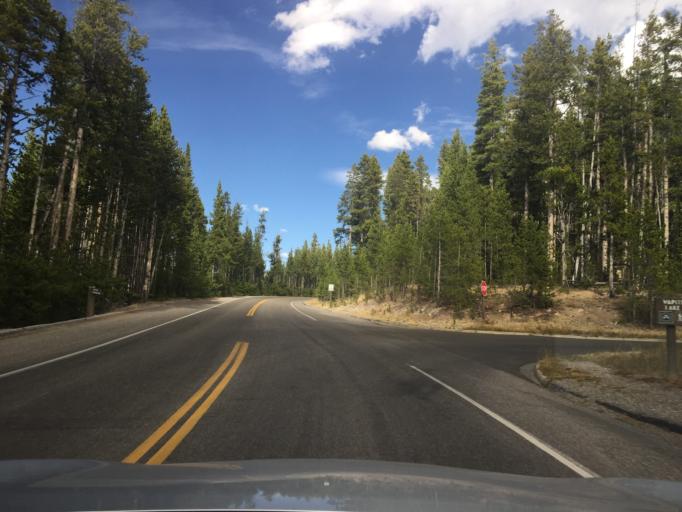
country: US
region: Montana
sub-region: Gallatin County
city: West Yellowstone
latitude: 44.7083
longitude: -110.5014
